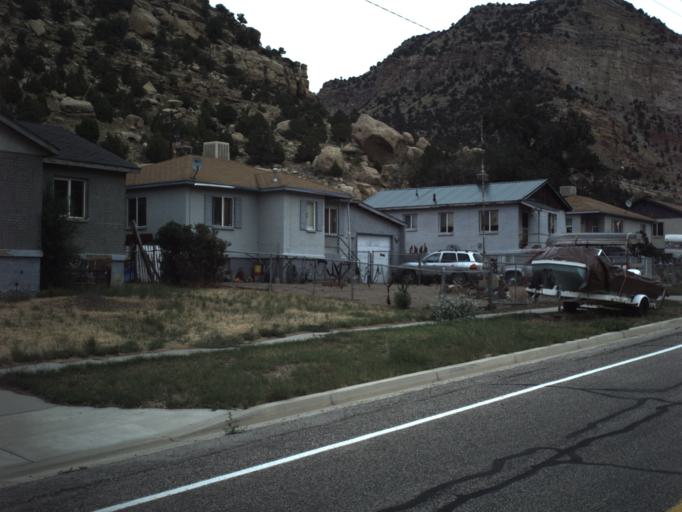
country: US
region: Utah
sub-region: Carbon County
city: East Carbon City
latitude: 39.5549
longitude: -110.3815
